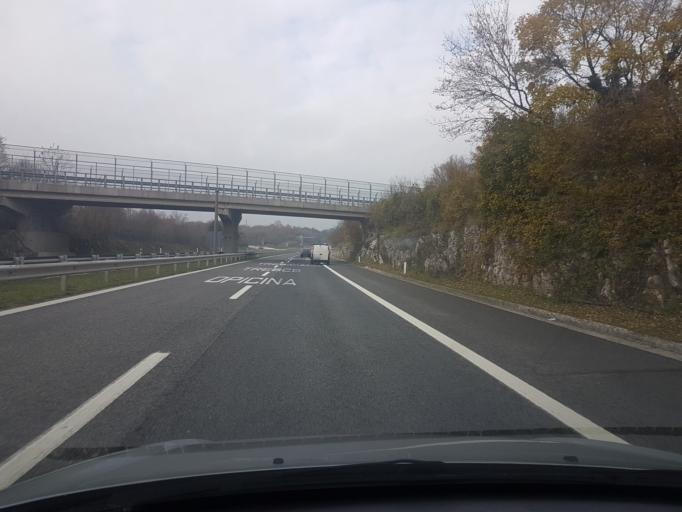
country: IT
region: Friuli Venezia Giulia
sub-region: Provincia di Trieste
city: Villa Opicina
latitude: 45.6716
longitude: 13.8215
